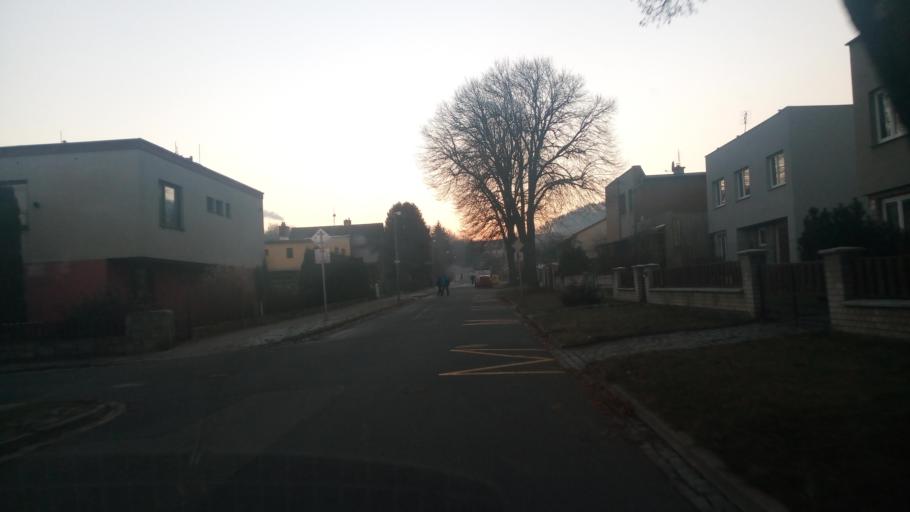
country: CZ
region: Olomoucky
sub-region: Okres Sumperk
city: Sumperk
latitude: 49.9636
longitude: 16.9608
